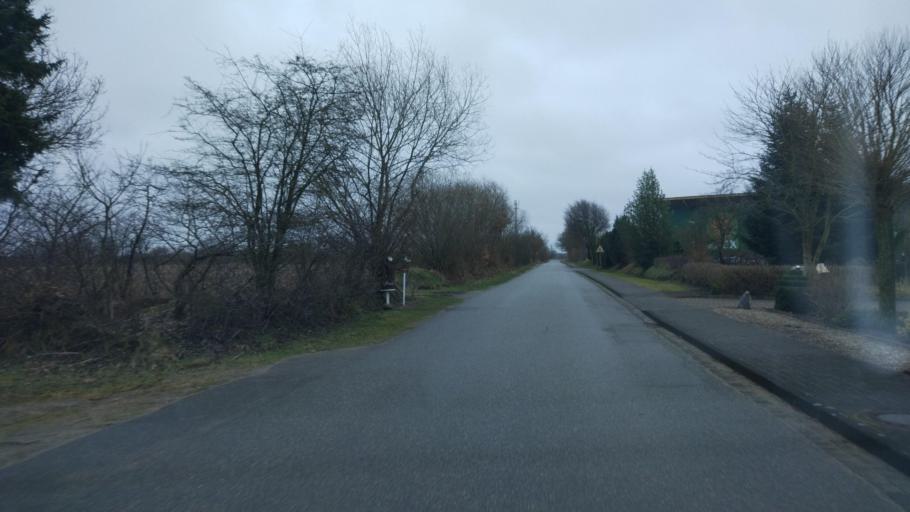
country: DE
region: Schleswig-Holstein
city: Ellingstedt
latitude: 54.4731
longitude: 9.4153
